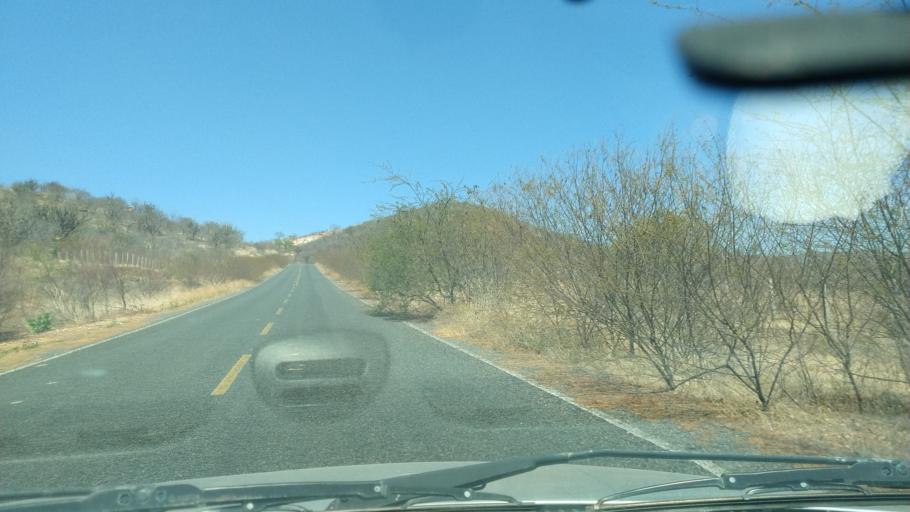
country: BR
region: Rio Grande do Norte
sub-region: Sao Tome
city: Sao Tome
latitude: -5.9698
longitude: -36.1545
